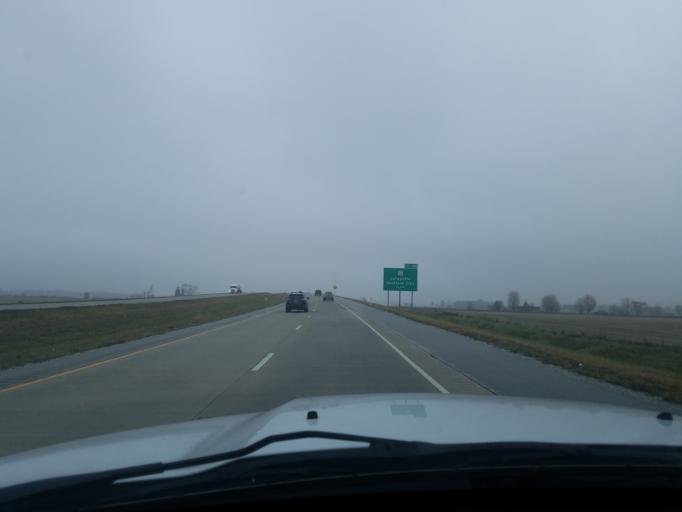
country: US
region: Indiana
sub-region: Howard County
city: Indian Heights
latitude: 40.4074
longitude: -86.1045
